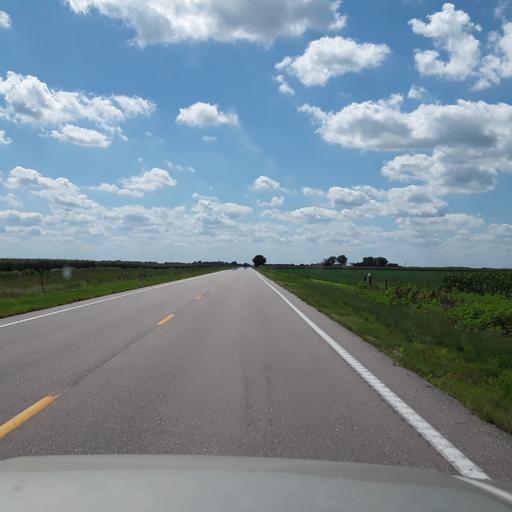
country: US
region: Nebraska
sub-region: Merrick County
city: Central City
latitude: 41.1914
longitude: -98.0673
